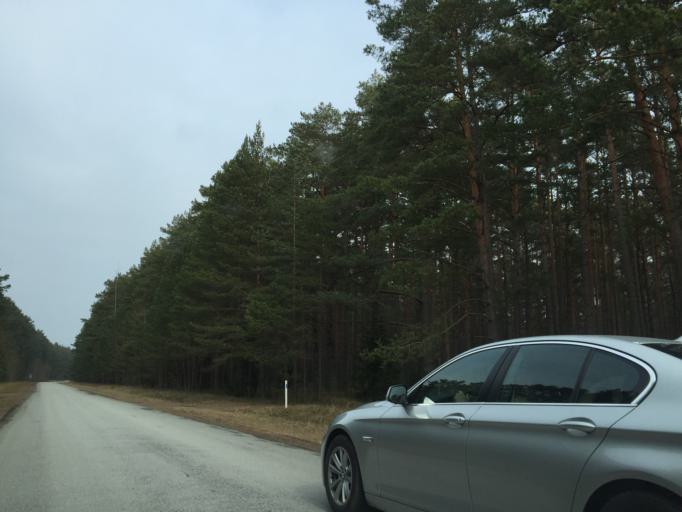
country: LV
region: Salacgrivas
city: Ainazi
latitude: 57.9427
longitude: 24.3916
